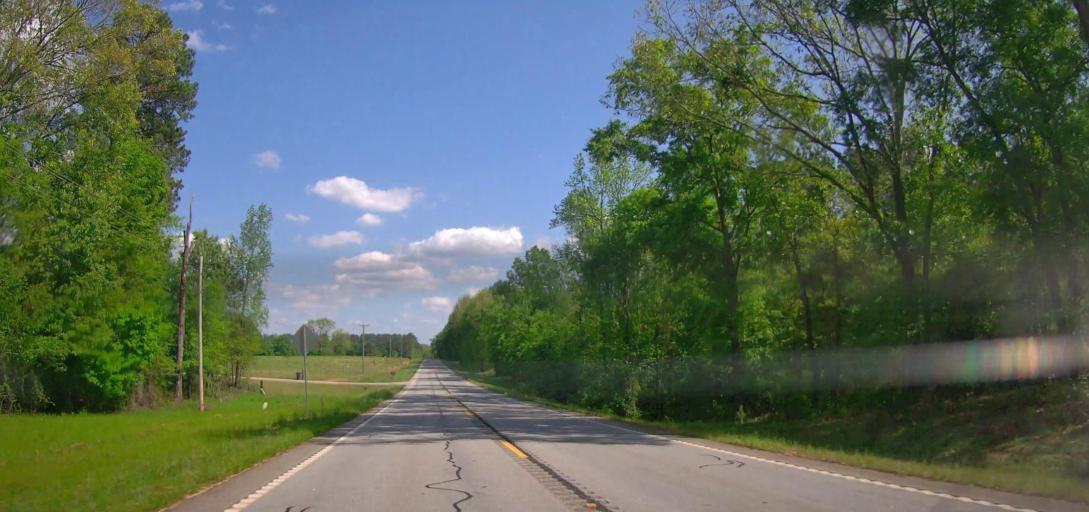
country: US
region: Georgia
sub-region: Greene County
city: Greensboro
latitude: 33.5931
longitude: -83.2904
